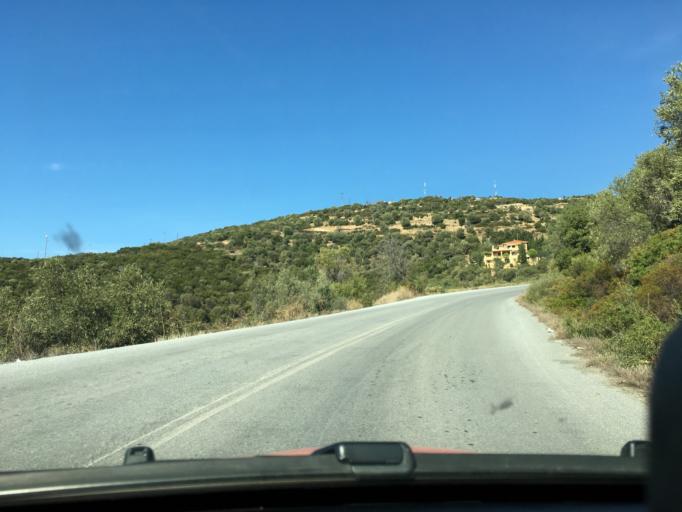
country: GR
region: Central Macedonia
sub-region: Nomos Chalkidikis
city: Agios Nikolaos
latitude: 40.3429
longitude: 23.7196
